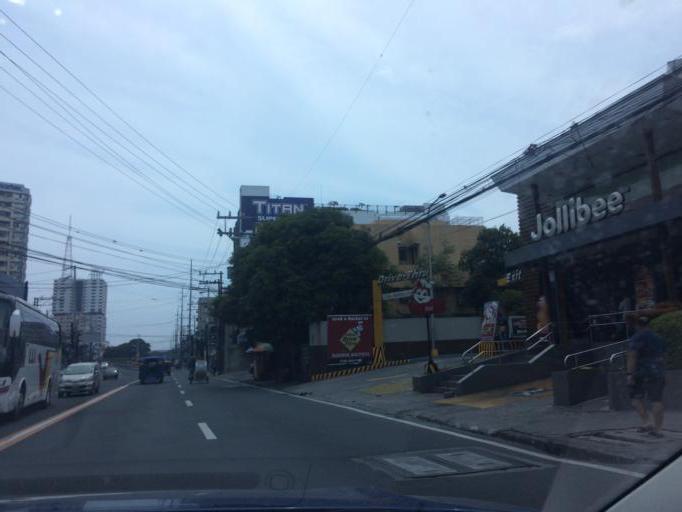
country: PH
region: Metro Manila
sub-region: Makati City
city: Makati City
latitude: 14.5555
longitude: 121.0022
